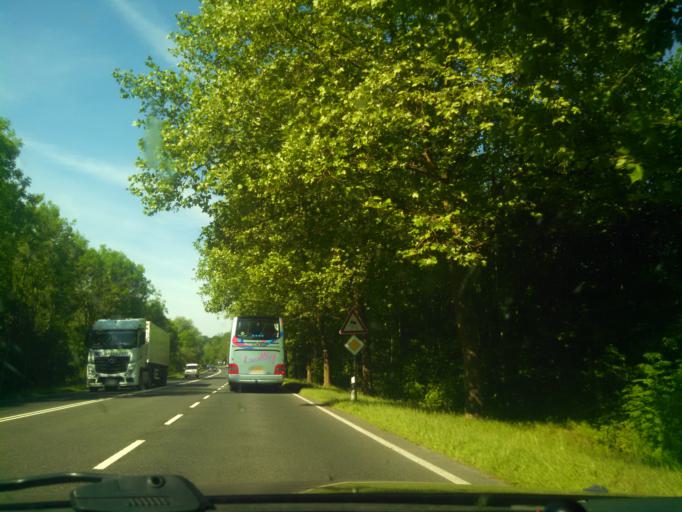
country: LU
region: Grevenmacher
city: Gonderange
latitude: 49.6873
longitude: 6.2313
